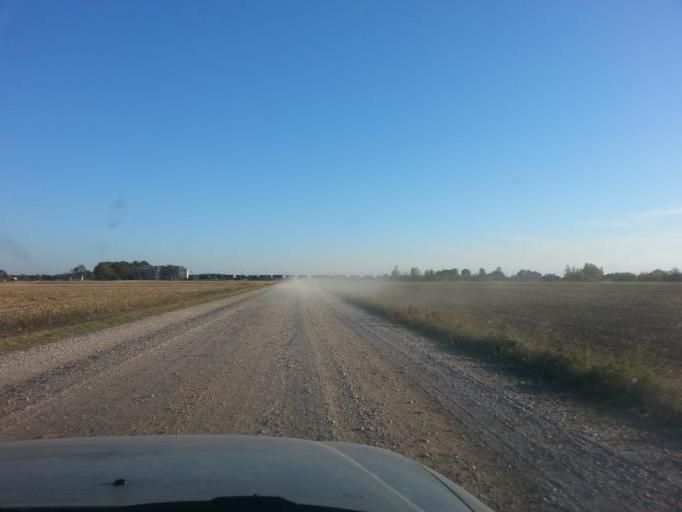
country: LV
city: Tervete
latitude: 56.6040
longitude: 23.4873
